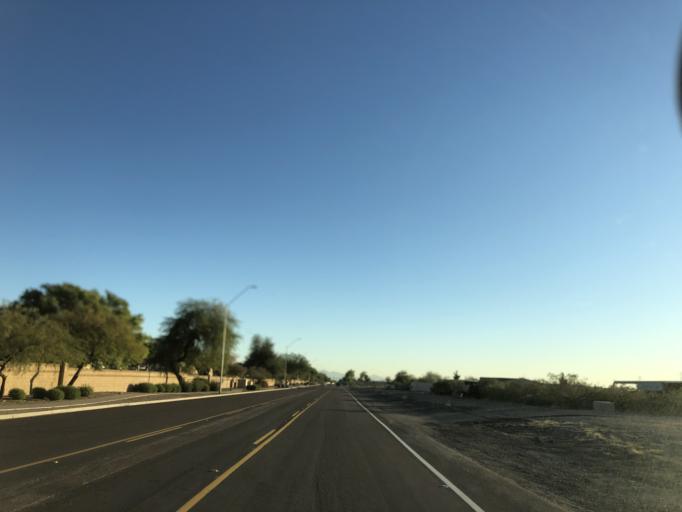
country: US
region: Arizona
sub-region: Maricopa County
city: Sun City West
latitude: 33.6946
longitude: -112.2897
